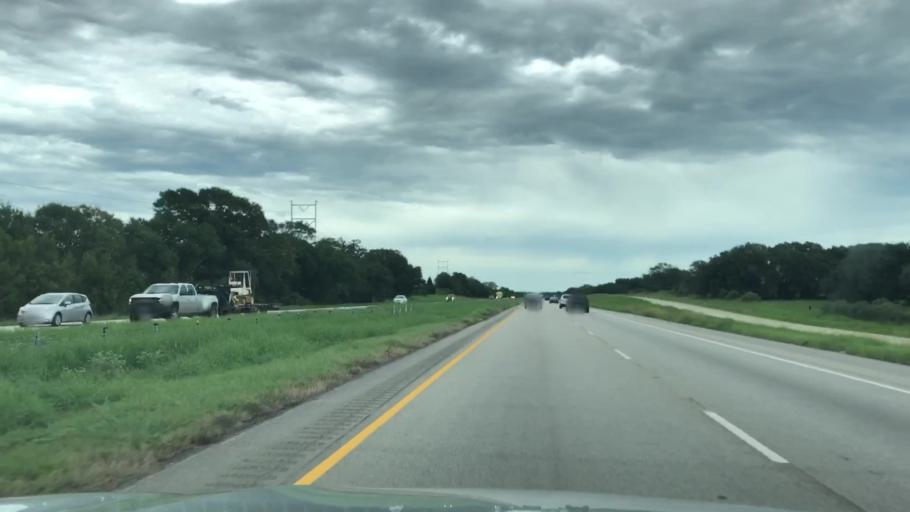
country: US
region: Texas
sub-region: Colorado County
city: Weimar
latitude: 29.6902
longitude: -96.6714
